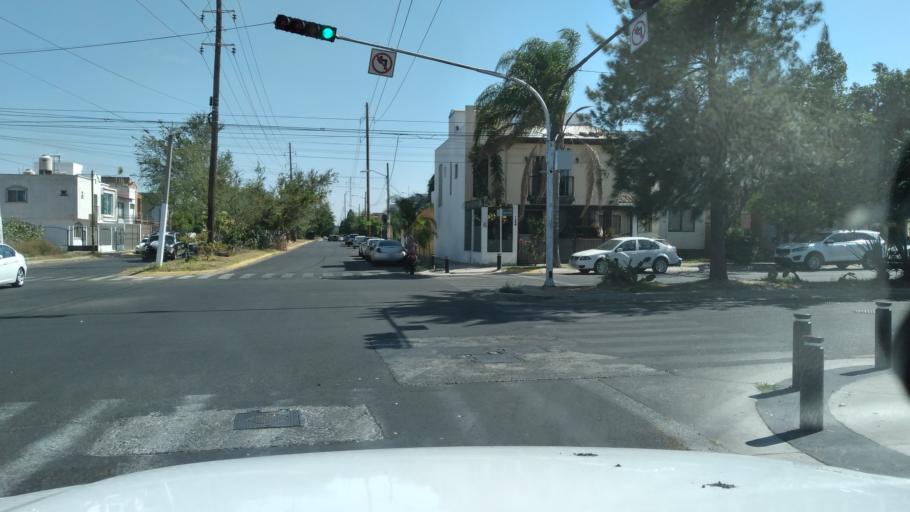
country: MX
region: Jalisco
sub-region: Zapopan
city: Zapopan
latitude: 20.7315
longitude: -103.3770
